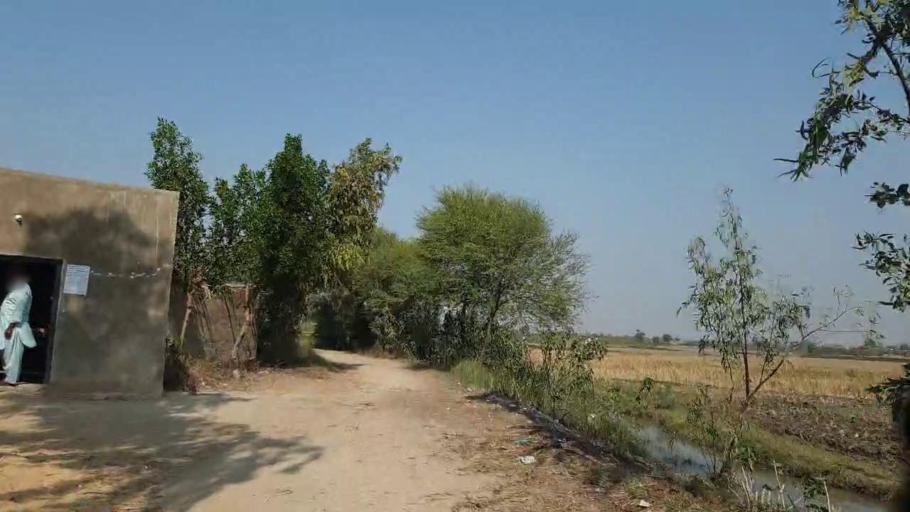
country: PK
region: Sindh
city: Tando Muhammad Khan
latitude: 25.0263
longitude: 68.4088
